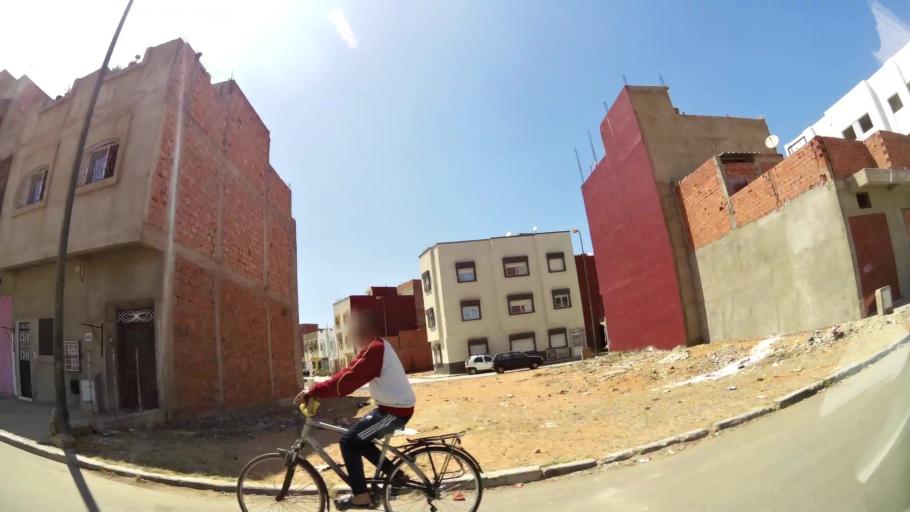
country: MA
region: Gharb-Chrarda-Beni Hssen
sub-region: Kenitra Province
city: Kenitra
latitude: 34.2427
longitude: -6.5393
